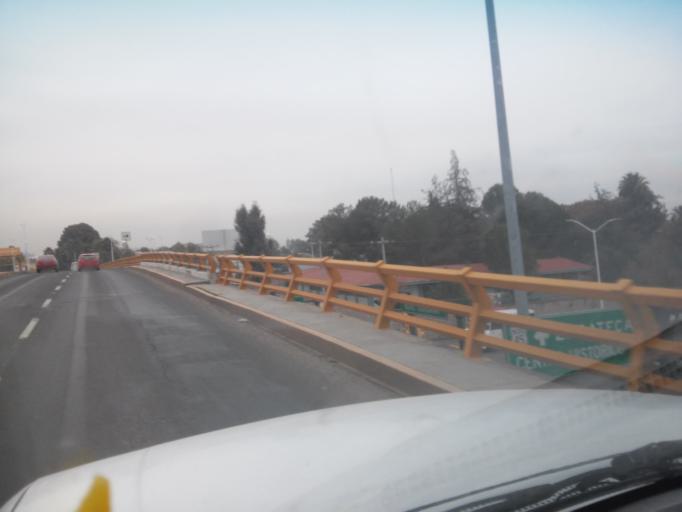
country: MX
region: Durango
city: Victoria de Durango
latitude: 24.0295
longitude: -104.6871
